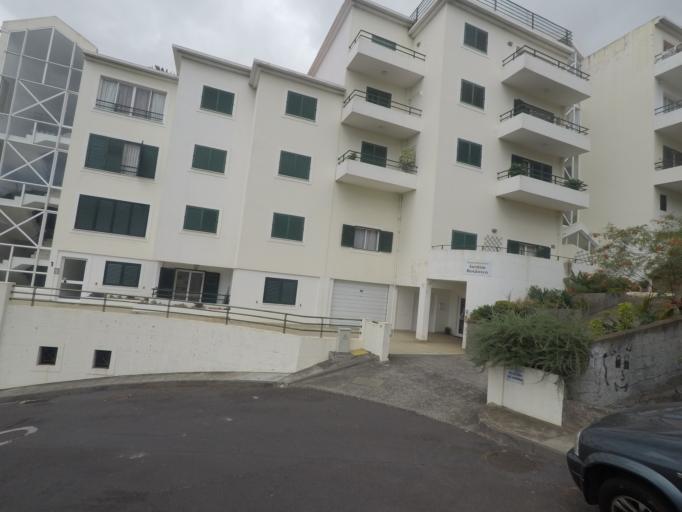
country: PT
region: Madeira
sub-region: Funchal
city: Nossa Senhora do Monte
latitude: 32.6613
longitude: -16.8920
